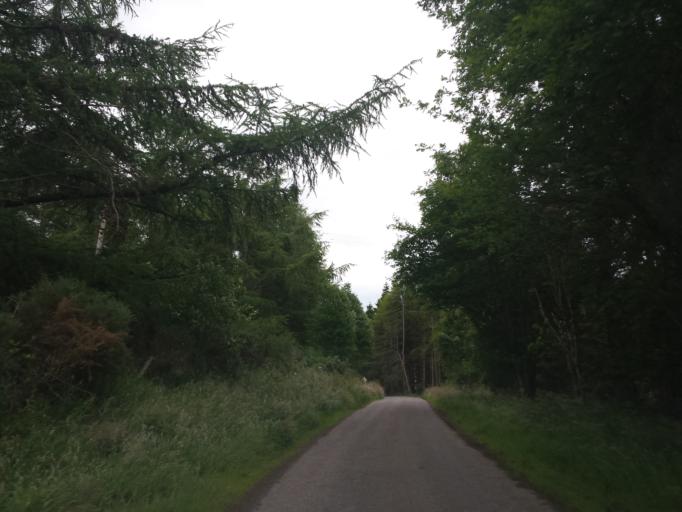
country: GB
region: Scotland
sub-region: Highland
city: Fortrose
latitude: 57.5115
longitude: -4.0269
